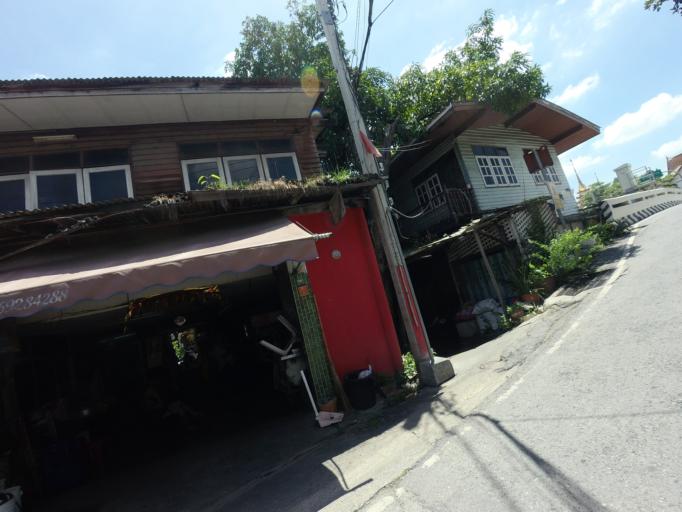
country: TH
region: Bangkok
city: Lat Phrao
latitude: 13.8028
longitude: 100.5881
